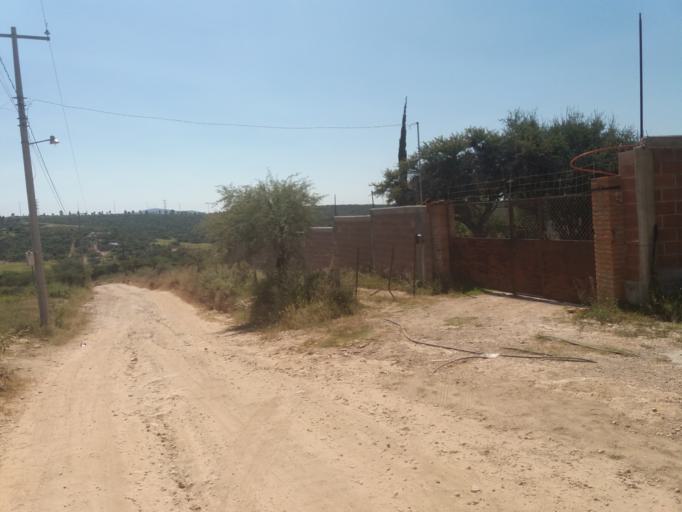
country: MX
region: Aguascalientes
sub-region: Aguascalientes
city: San Sebastian [Fraccionamiento]
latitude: 21.7708
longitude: -102.2349
